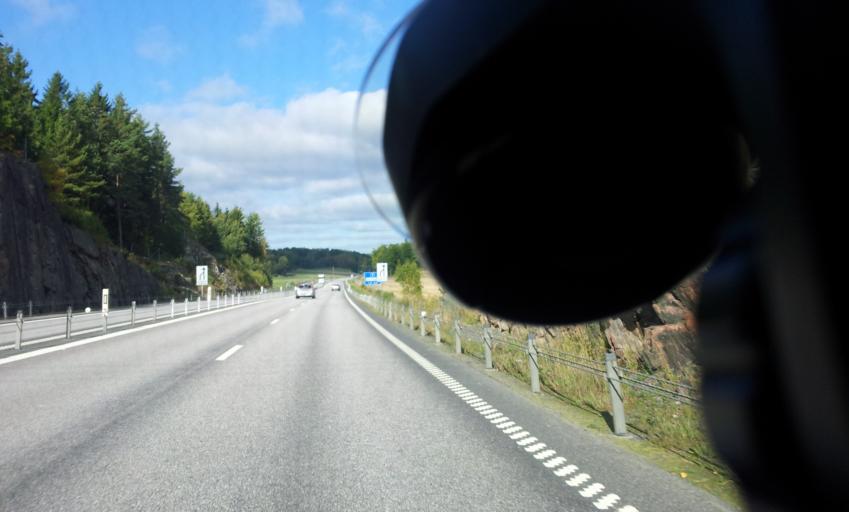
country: SE
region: OEstergoetland
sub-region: Valdemarsviks Kommun
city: Gusum
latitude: 58.3091
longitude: 16.4841
